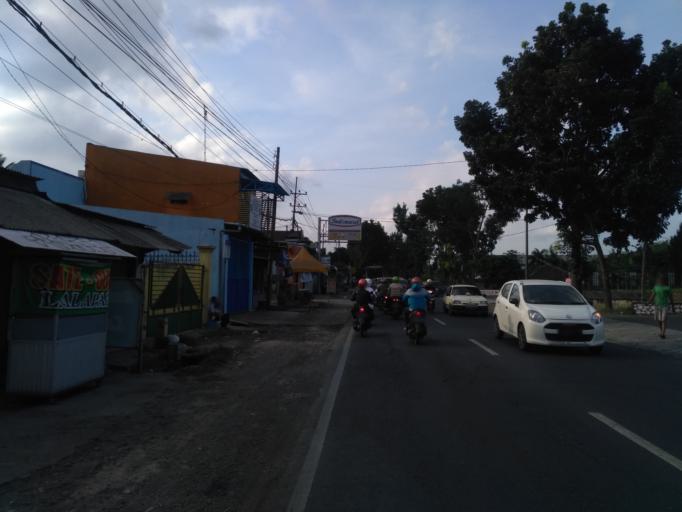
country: ID
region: East Java
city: Wadung
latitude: -8.0450
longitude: 112.6078
